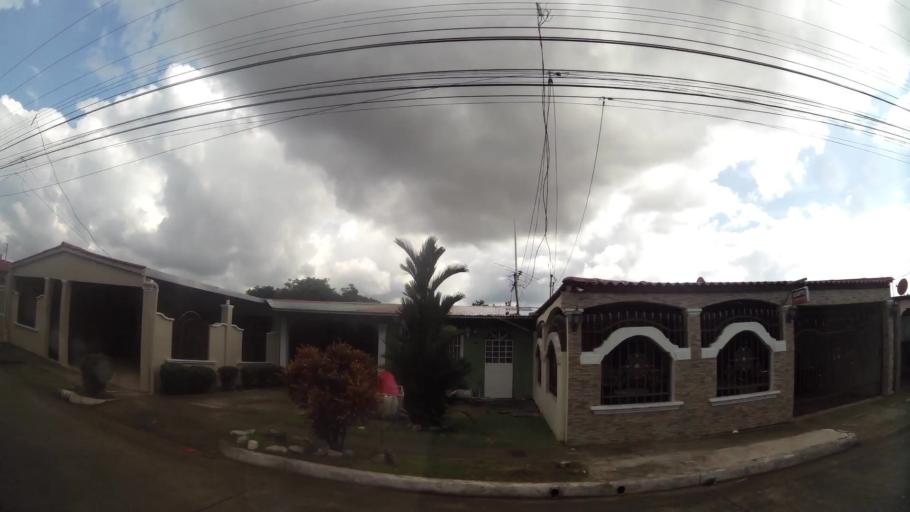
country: PA
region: Panama
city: Nuevo Arraijan
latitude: 8.9350
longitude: -79.7393
